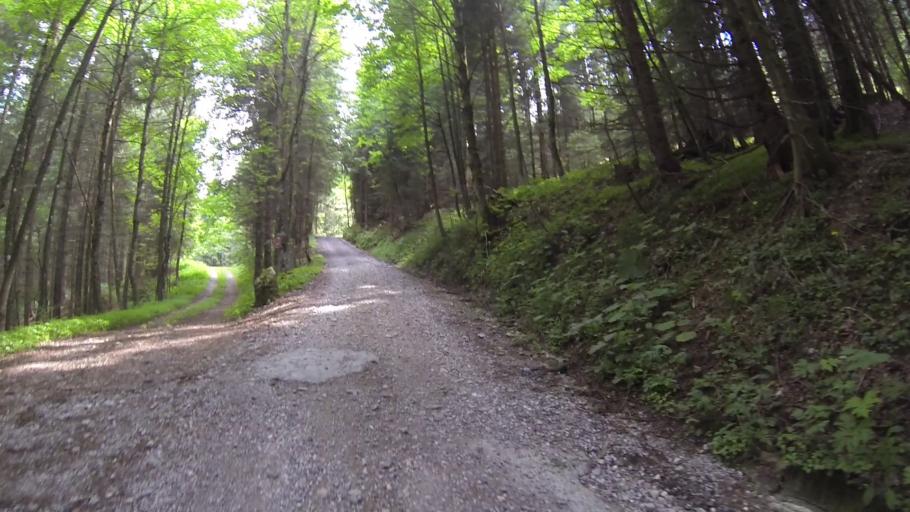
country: AT
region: Tyrol
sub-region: Politischer Bezirk Reutte
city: Jungholz
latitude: 47.5954
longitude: 10.4727
